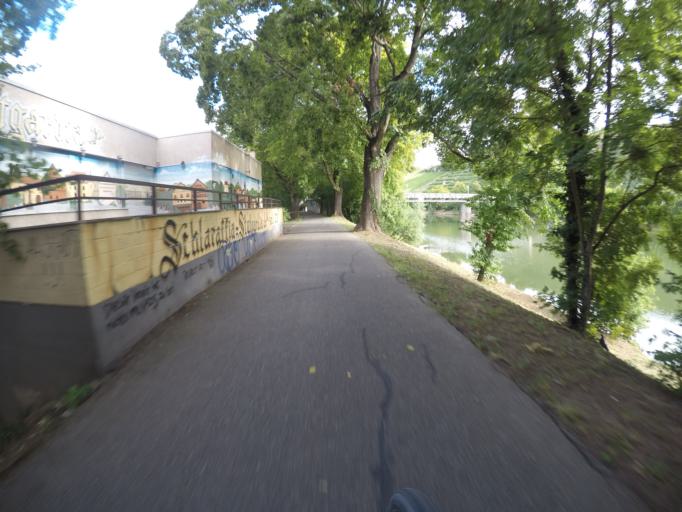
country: DE
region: Baden-Wuerttemberg
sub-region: Regierungsbezirk Stuttgart
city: Stuttgart Muehlhausen
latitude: 48.8193
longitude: 9.2273
